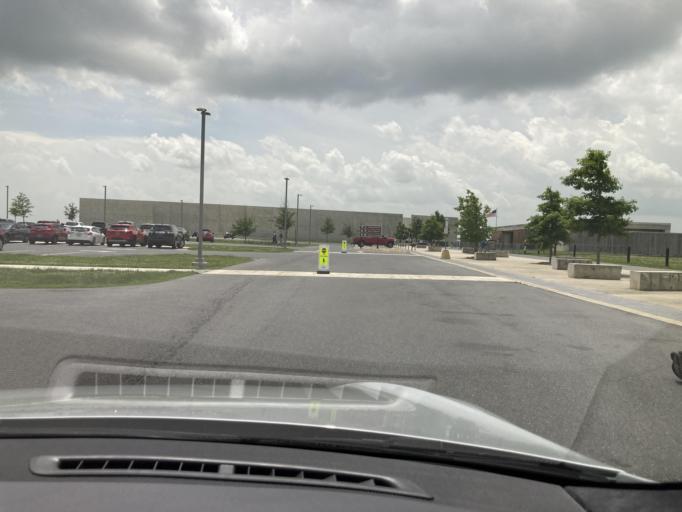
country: US
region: Pennsylvania
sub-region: Somerset County
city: Friedens
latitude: 40.0579
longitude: -78.9064
